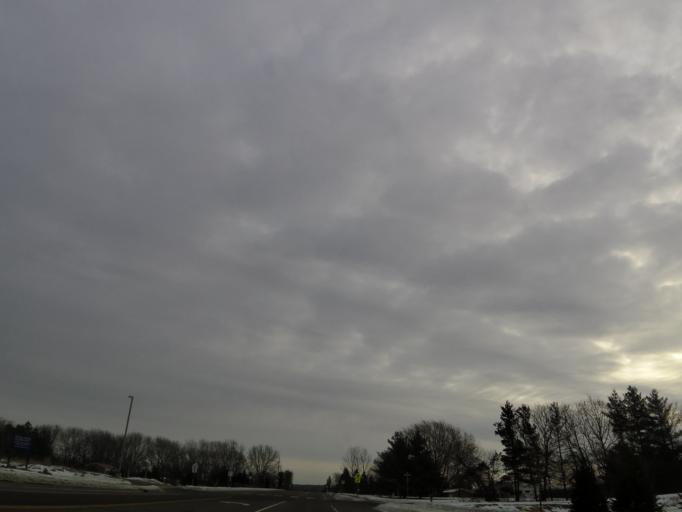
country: US
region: Minnesota
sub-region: Scott County
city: Prior Lake
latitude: 44.7247
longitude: -93.3633
